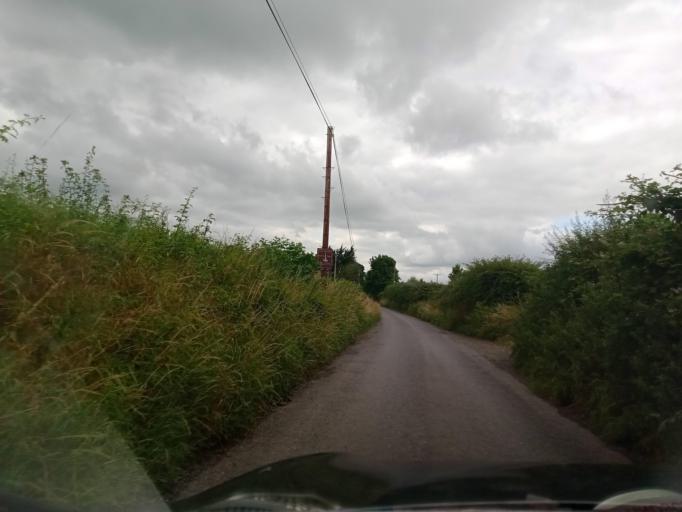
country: IE
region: Leinster
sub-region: Laois
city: Stradbally
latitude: 52.9597
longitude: -7.1965
